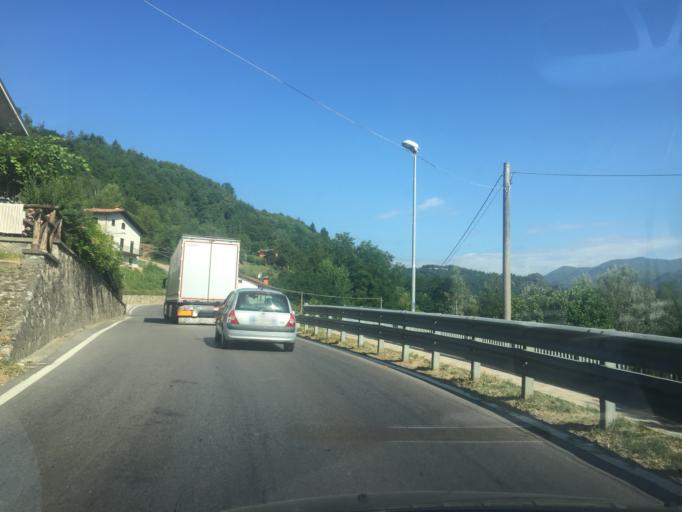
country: IT
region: Tuscany
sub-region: Provincia di Lucca
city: Villa Collemandina
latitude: 44.1364
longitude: 10.3692
